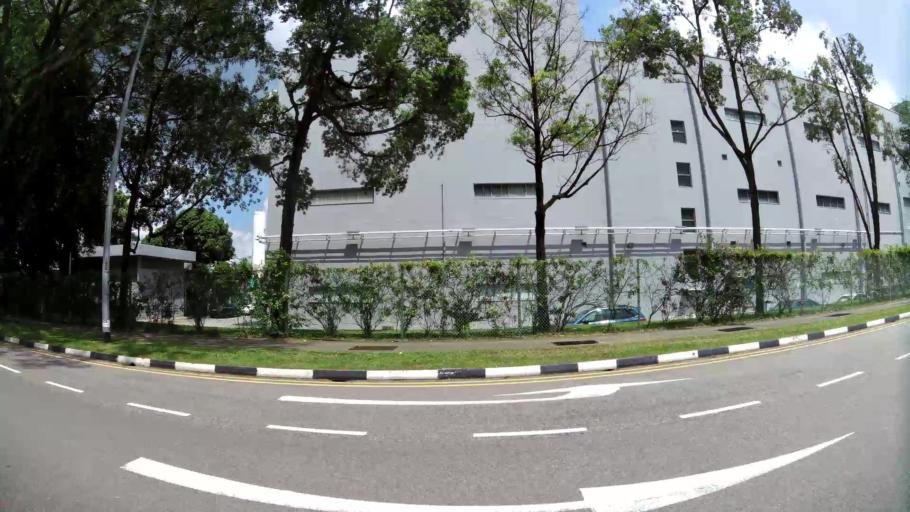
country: MY
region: Johor
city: Kampung Pasir Gudang Baru
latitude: 1.4391
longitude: 103.8326
